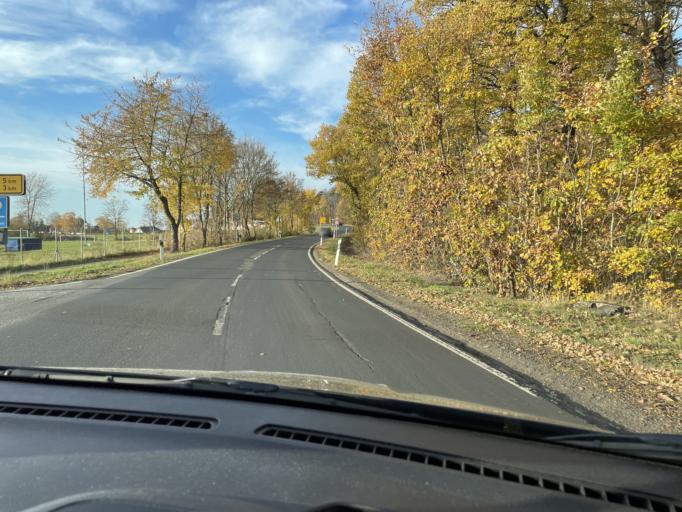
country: DE
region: Hesse
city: Gross-Umstadt
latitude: 49.8178
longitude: 8.9274
